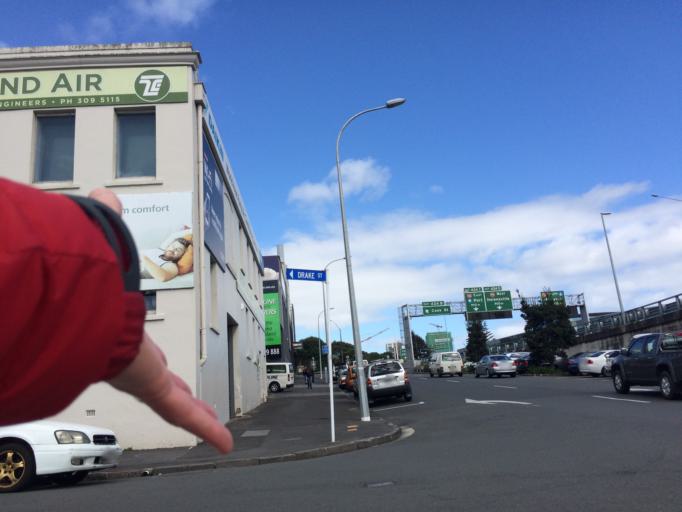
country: NZ
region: Auckland
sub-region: Auckland
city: Auckland
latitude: -36.8488
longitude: 174.7536
